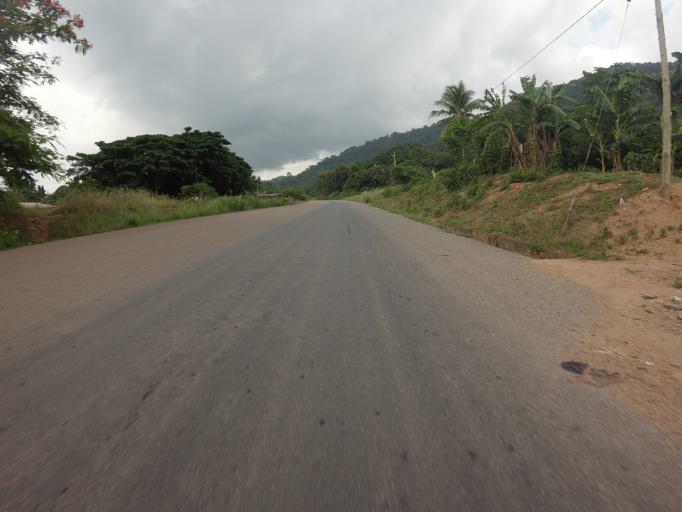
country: GH
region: Volta
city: Kpandu
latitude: 6.9134
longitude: 0.4519
